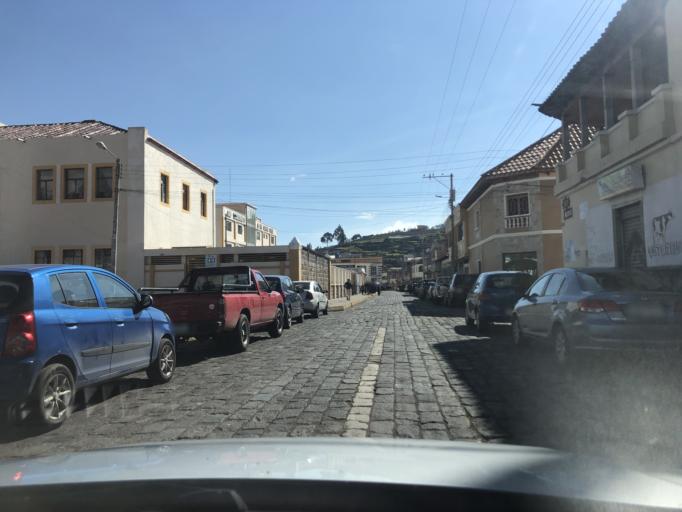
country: EC
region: Chimborazo
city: Riobamba
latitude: -1.7020
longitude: -78.7733
